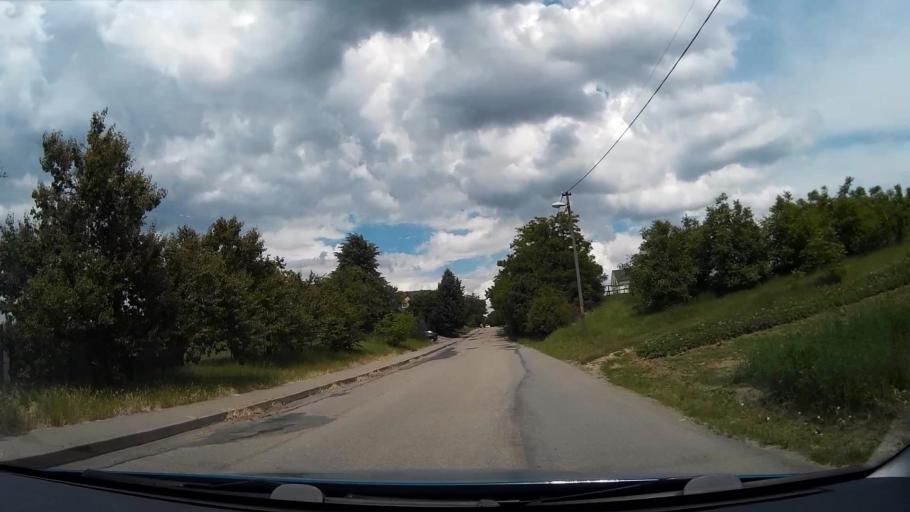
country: CZ
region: South Moravian
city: Orechov
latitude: 49.1131
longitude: 16.5254
